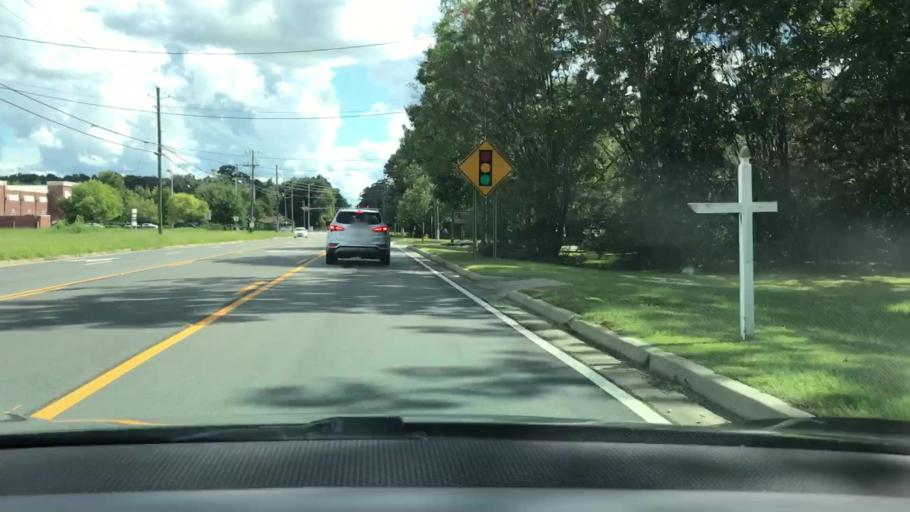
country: US
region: Alabama
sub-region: Montgomery County
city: Pike Road
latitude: 32.3488
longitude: -86.0951
